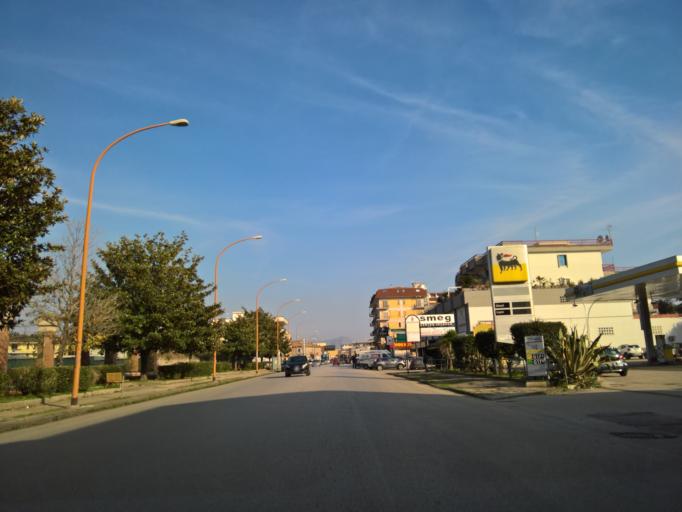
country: IT
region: Campania
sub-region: Provincia di Caserta
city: San Prisco
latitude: 41.0817
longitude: 14.2675
